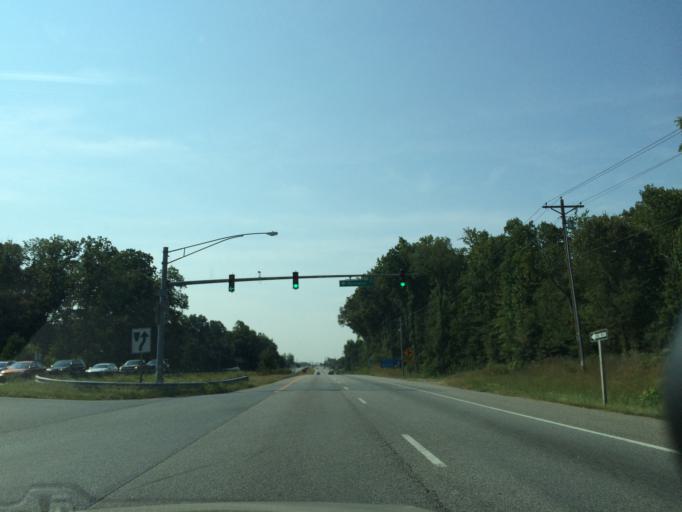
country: US
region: Maryland
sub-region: Charles County
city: La Plata
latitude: 38.5556
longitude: -76.9865
